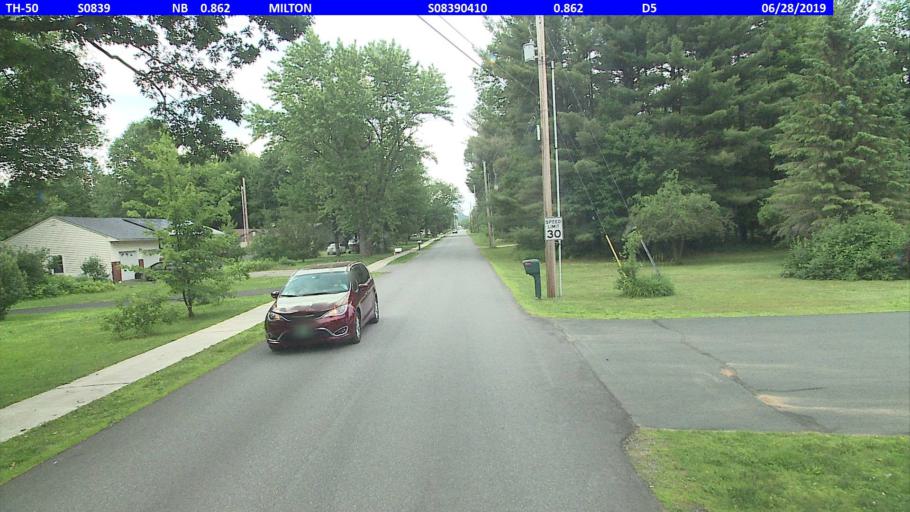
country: US
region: Vermont
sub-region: Chittenden County
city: Milton
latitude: 44.6168
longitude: -73.1110
